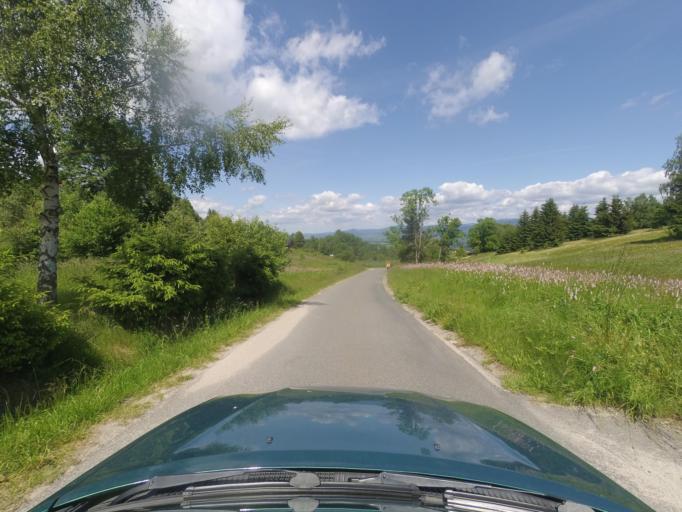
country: PL
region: Lower Silesian Voivodeship
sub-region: Powiat klodzki
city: Miedzylesie
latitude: 50.1172
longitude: 16.6316
